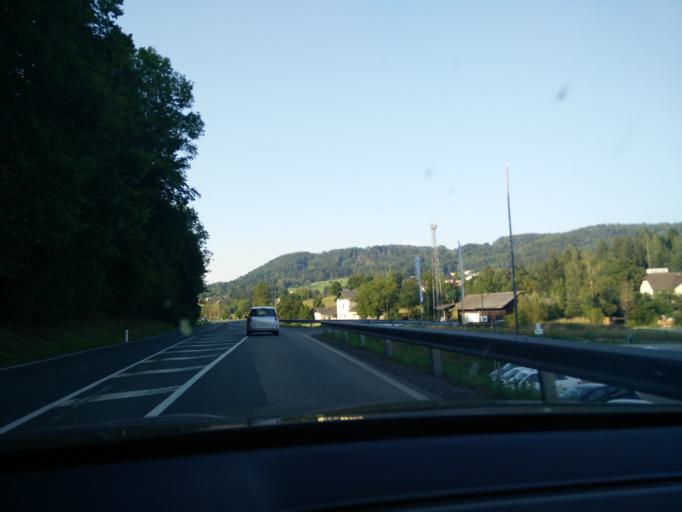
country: AT
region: Carinthia
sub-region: Politischer Bezirk Klagenfurt Land
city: Maria Rain
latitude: 46.5622
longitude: 14.2828
